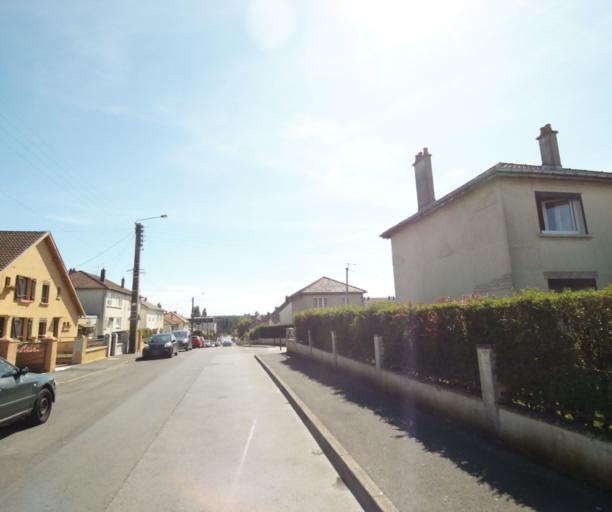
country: FR
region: Champagne-Ardenne
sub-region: Departement des Ardennes
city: Charleville-Mezieres
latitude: 49.7488
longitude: 4.7151
